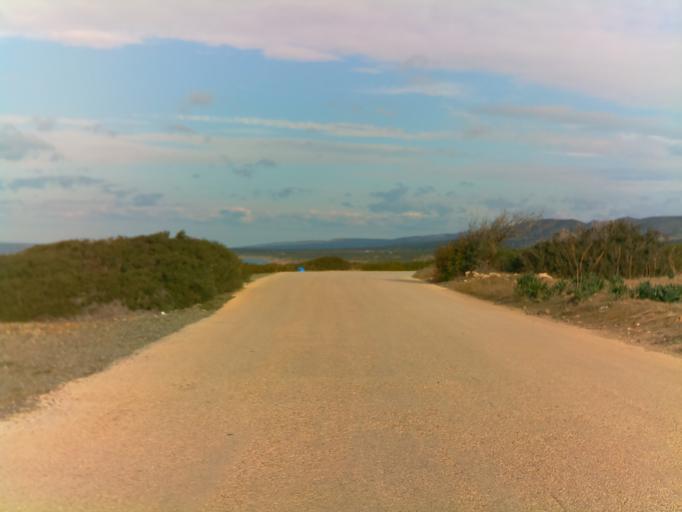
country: CY
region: Pafos
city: Pegeia
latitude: 34.9093
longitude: 32.3265
